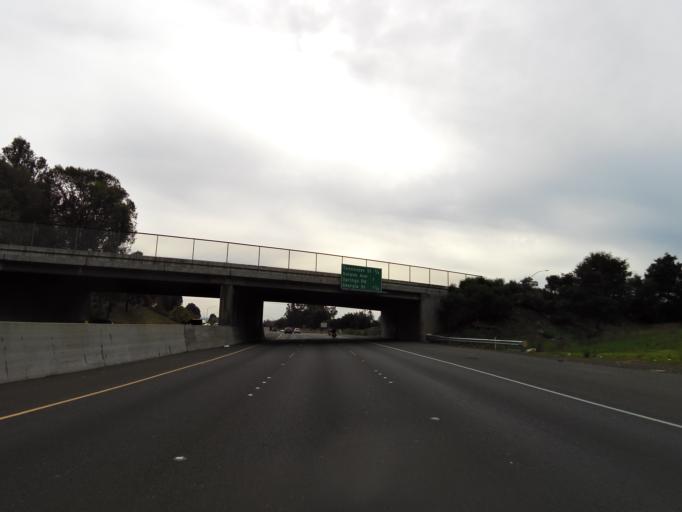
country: US
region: California
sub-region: Solano County
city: Vallejo
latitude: 38.1239
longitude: -122.2300
